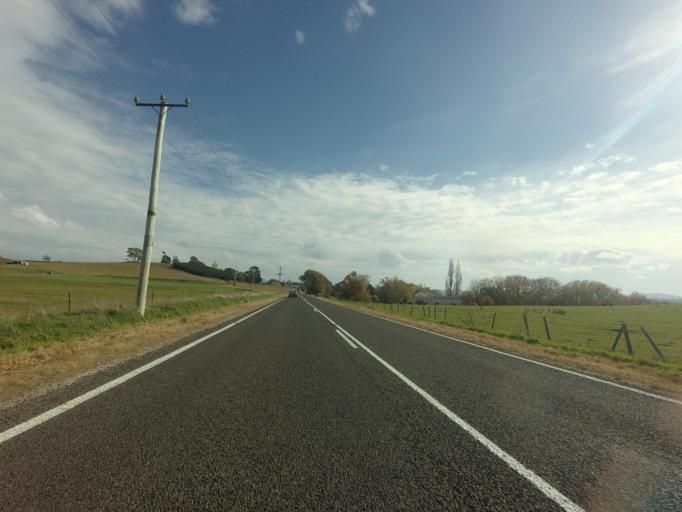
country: AU
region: Tasmania
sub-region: Meander Valley
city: Deloraine
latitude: -41.5255
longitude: 146.6956
